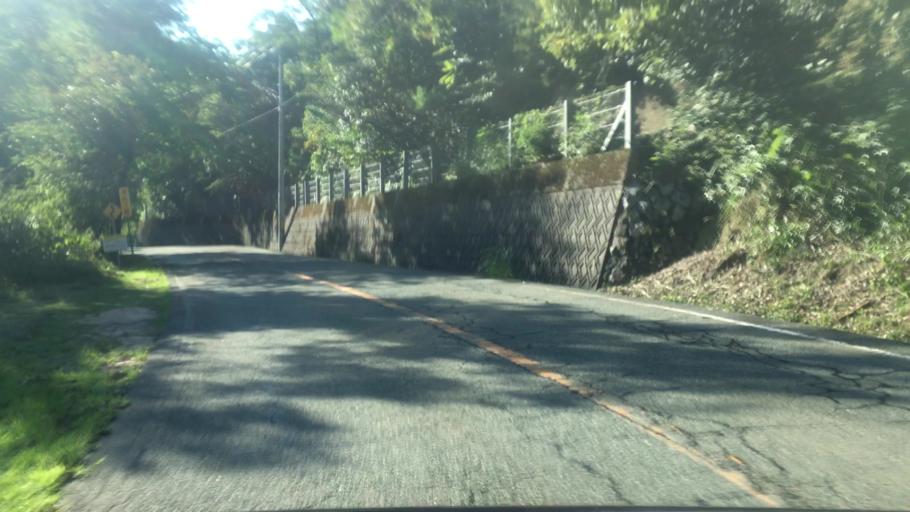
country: JP
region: Hyogo
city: Toyooka
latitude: 35.6192
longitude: 134.8724
